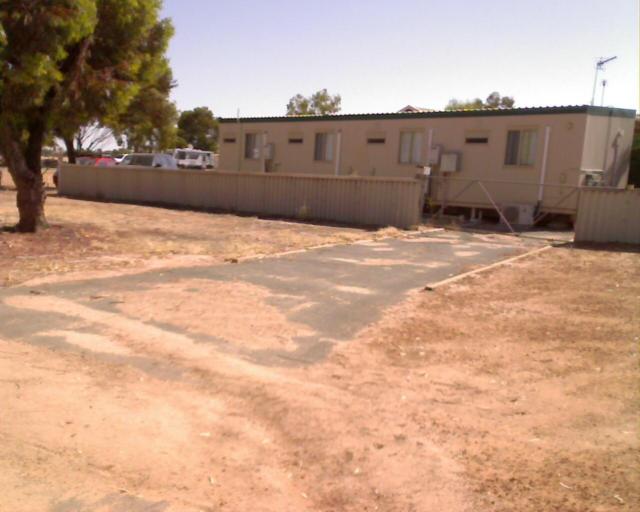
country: AU
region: Western Australia
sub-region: Cunderdin
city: Cunderdin
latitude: -31.6243
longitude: 117.7165
